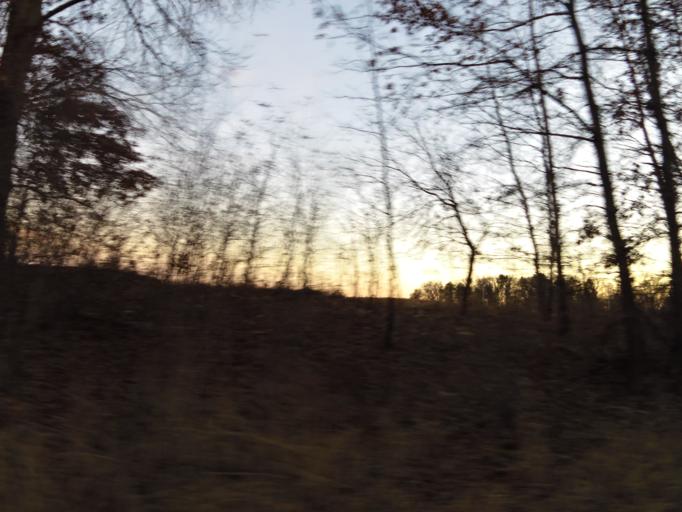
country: US
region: Minnesota
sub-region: Washington County
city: Grant
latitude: 45.1153
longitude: -92.8495
